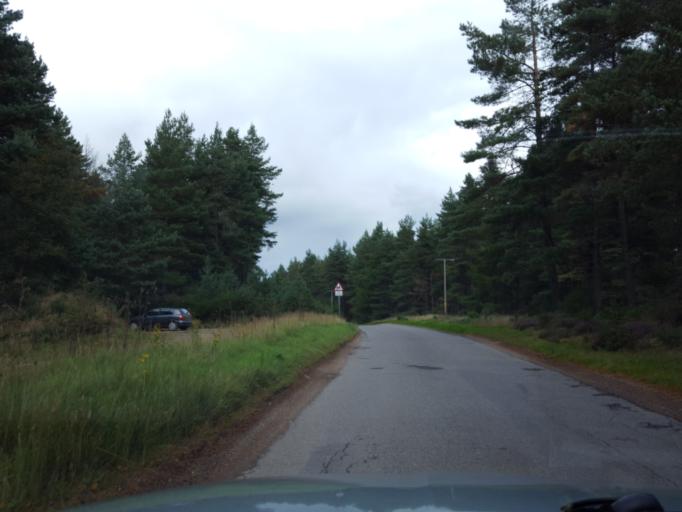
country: GB
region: Scotland
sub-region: Aberdeenshire
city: Banchory
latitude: 56.9924
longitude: -2.5778
